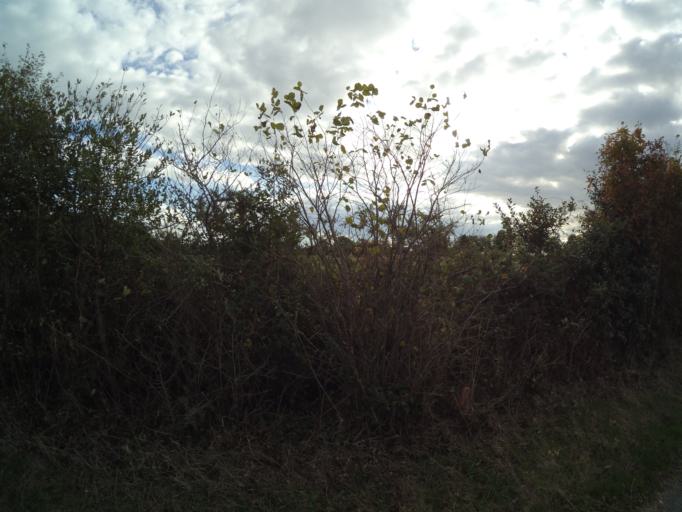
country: FR
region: Pays de la Loire
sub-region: Departement de la Loire-Atlantique
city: Maisdon-sur-Sevre
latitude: 47.0821
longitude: -1.3609
